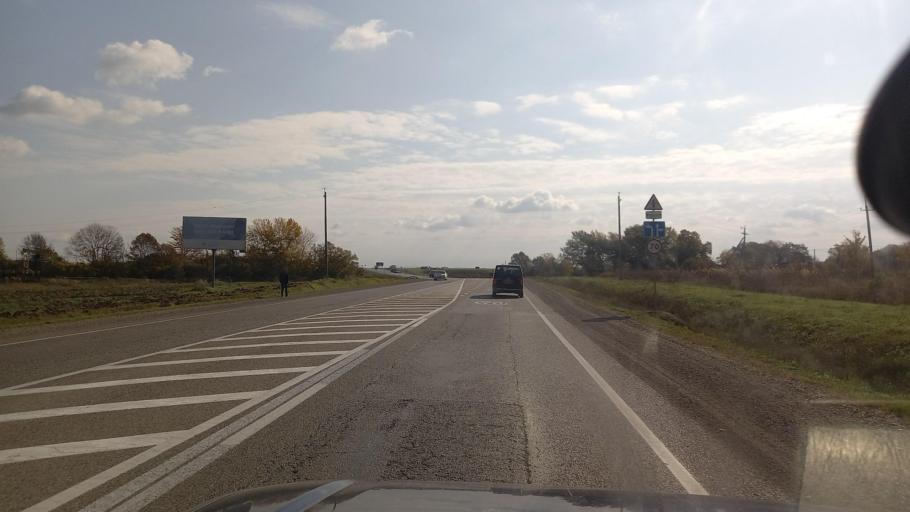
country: RU
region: Krasnodarskiy
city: Abinsk
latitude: 44.8755
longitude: 38.1096
